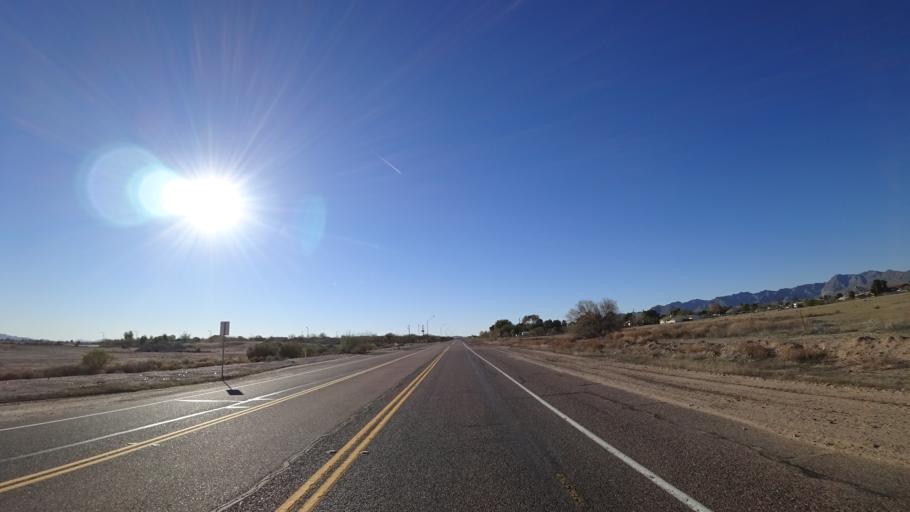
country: US
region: Arizona
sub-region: Maricopa County
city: Citrus Park
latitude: 33.4502
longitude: -112.4680
